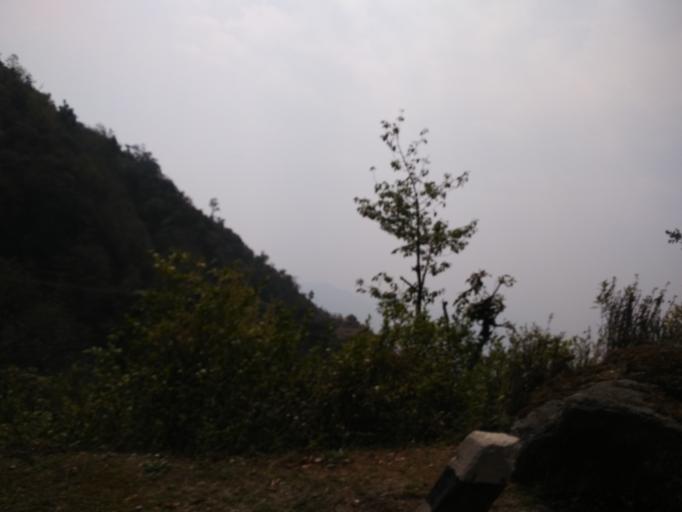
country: NP
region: Central Region
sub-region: Narayani Zone
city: Hitura
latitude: 27.5636
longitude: 85.0746
